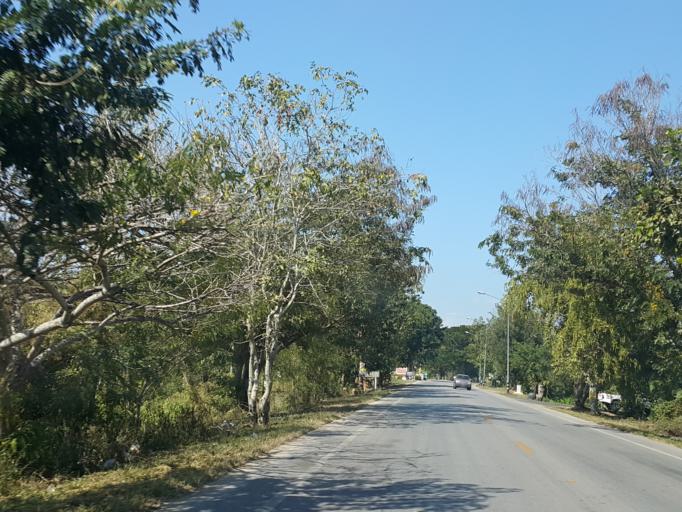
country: TH
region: Chiang Mai
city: Mae Taeng
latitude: 19.0486
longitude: 98.9633
